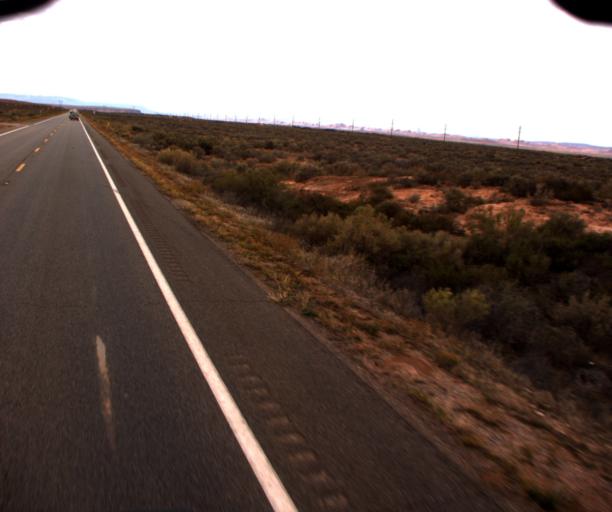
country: US
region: Arizona
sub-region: Navajo County
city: Kayenta
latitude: 36.8094
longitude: -109.9036
